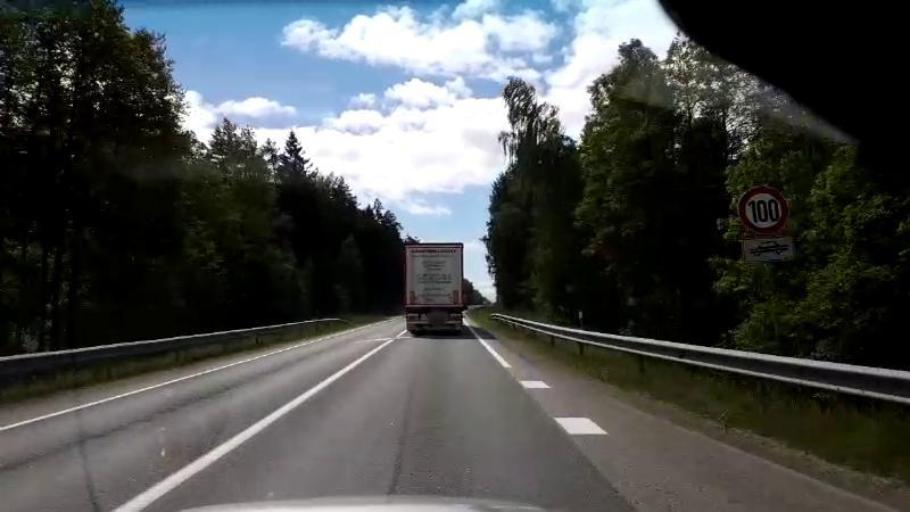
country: LV
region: Salacgrivas
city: Salacgriva
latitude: 57.5643
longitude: 24.4342
